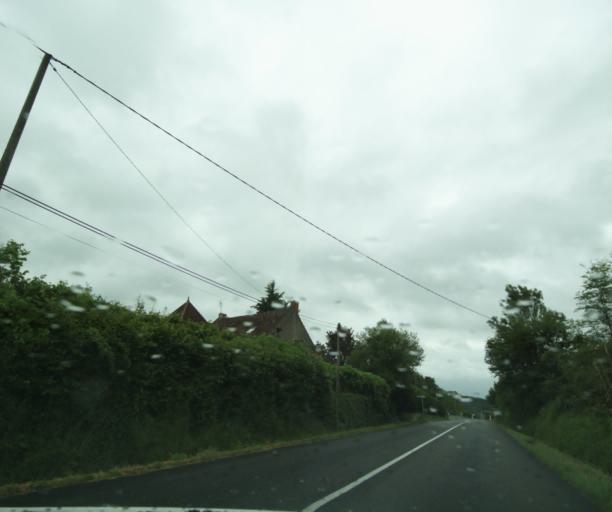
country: FR
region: Bourgogne
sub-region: Departement de Saone-et-Loire
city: Charolles
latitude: 46.4877
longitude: 4.2705
